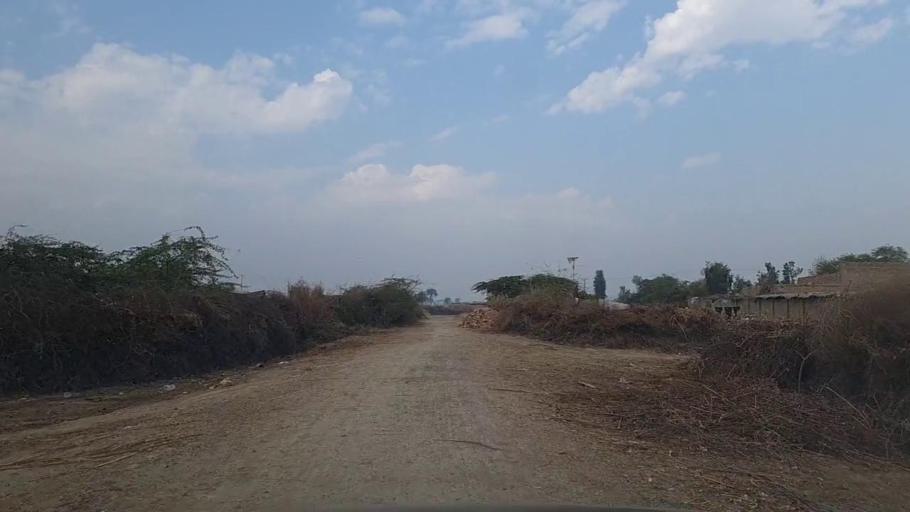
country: PK
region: Sindh
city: Daur
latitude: 26.3728
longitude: 68.3895
